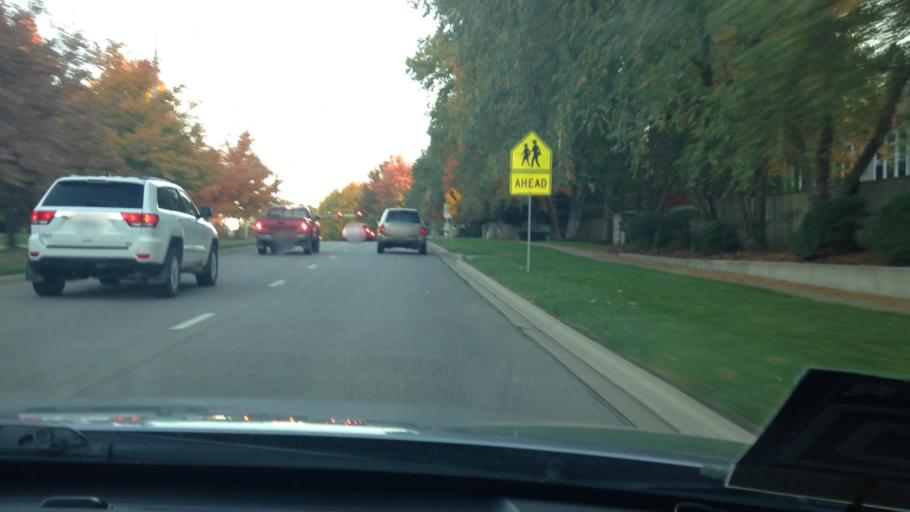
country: US
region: Kansas
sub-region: Johnson County
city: Lenexa
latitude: 38.8962
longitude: -94.7053
